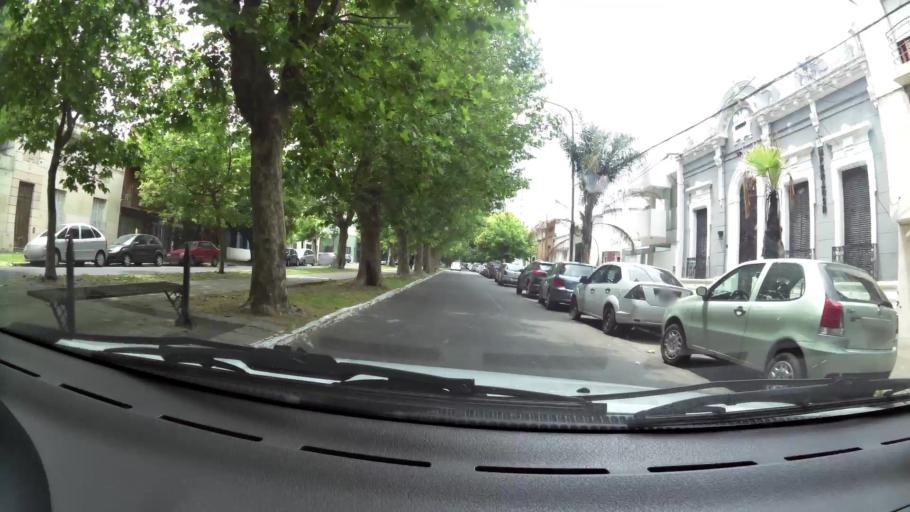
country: AR
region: Buenos Aires
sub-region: Partido de La Plata
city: La Plata
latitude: -34.9262
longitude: -57.9586
